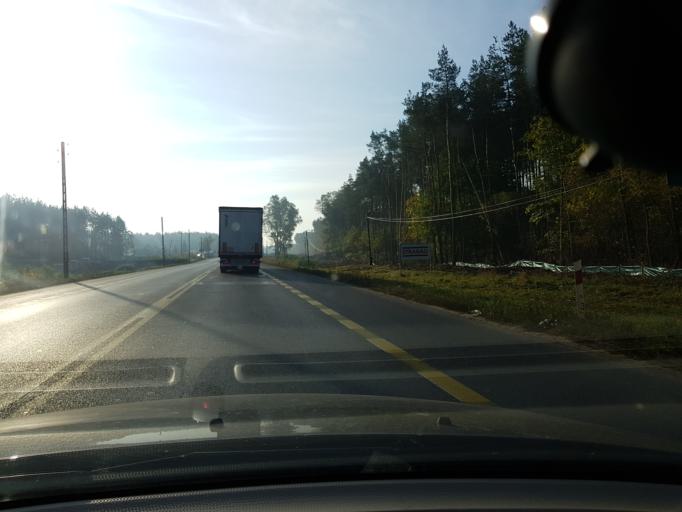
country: PL
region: Masovian Voivodeship
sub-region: Powiat otwocki
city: Otwock
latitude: 52.1456
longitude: 21.3237
